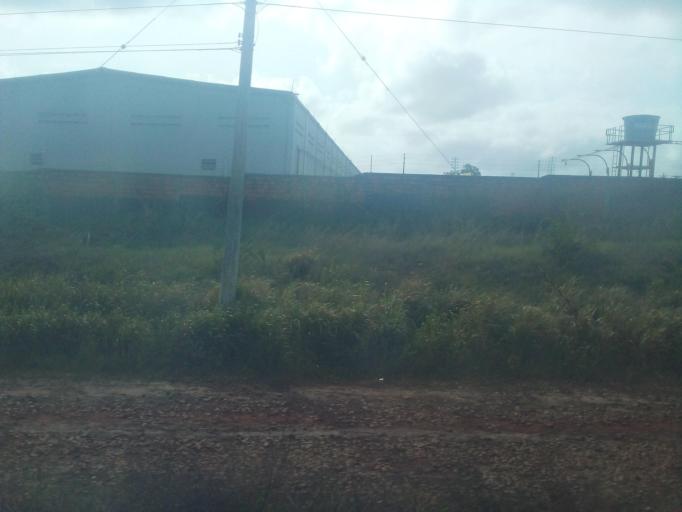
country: BR
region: Maranhao
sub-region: Sao Luis
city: Sao Luis
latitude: -2.7023
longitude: -44.3117
